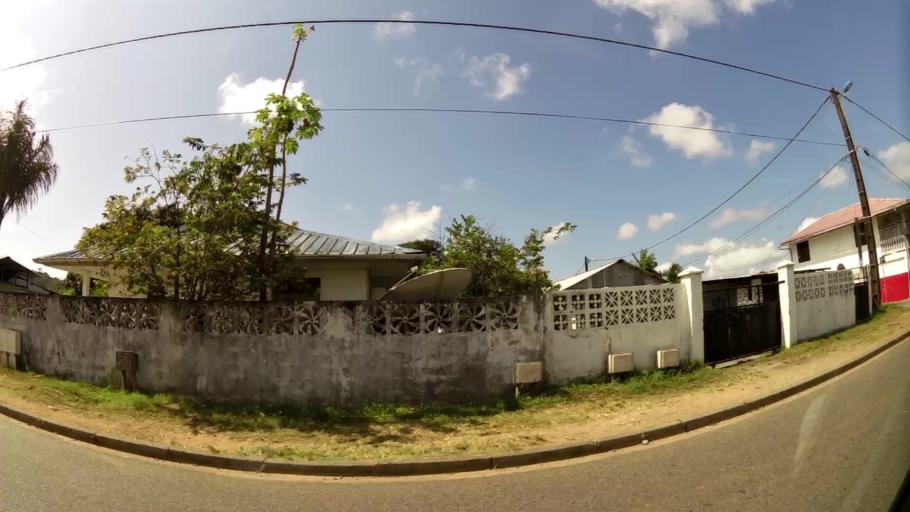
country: GF
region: Guyane
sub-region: Guyane
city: Cayenne
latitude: 4.9242
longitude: -52.3186
